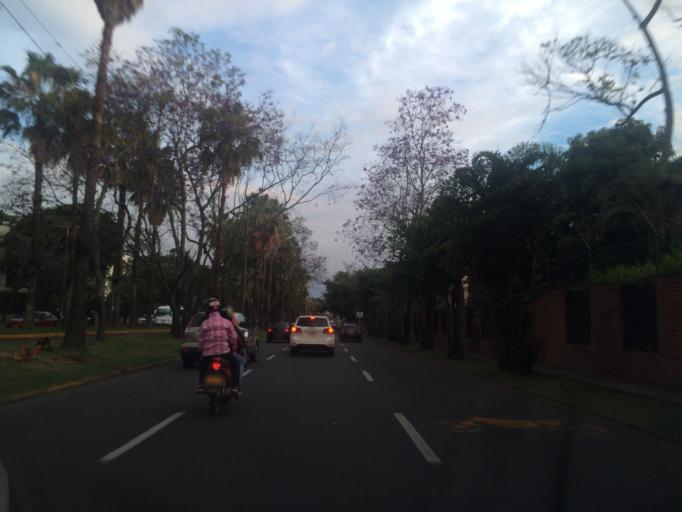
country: CO
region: Valle del Cauca
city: Cali
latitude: 3.3808
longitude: -76.5377
